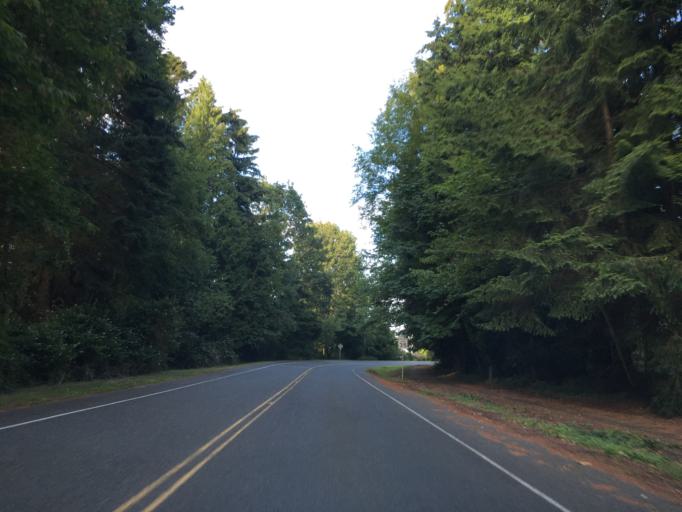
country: CA
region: British Columbia
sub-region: Greater Vancouver Regional District
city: White Rock
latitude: 48.9723
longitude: -122.7915
